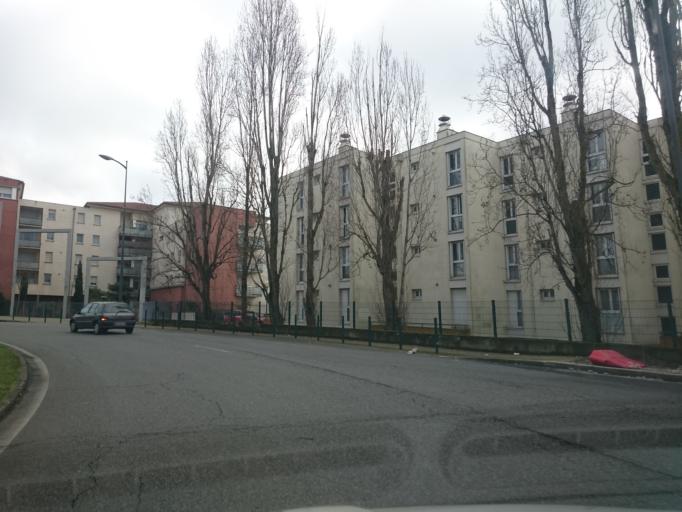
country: FR
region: Midi-Pyrenees
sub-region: Departement de la Haute-Garonne
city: Colomiers
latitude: 43.6086
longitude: 1.3268
